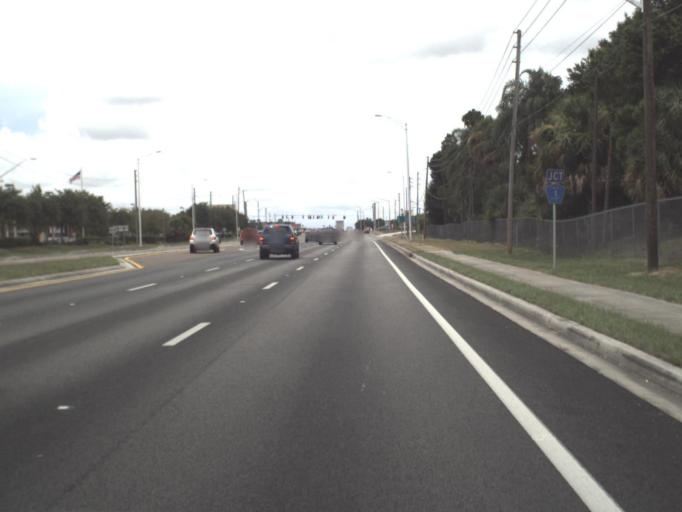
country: US
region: Florida
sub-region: Pasco County
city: Trinity
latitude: 28.2062
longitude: -82.6621
